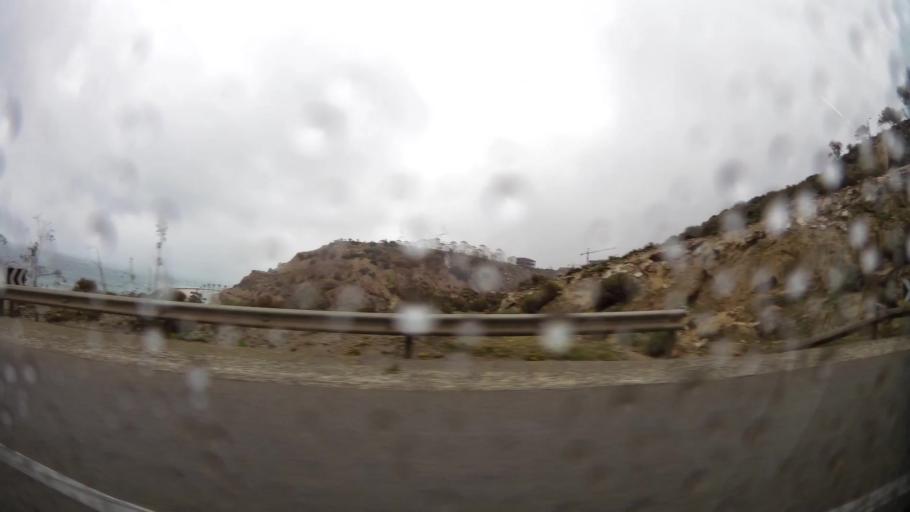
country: MA
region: Taza-Al Hoceima-Taounate
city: Tirhanimine
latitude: 35.2441
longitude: -3.9636
